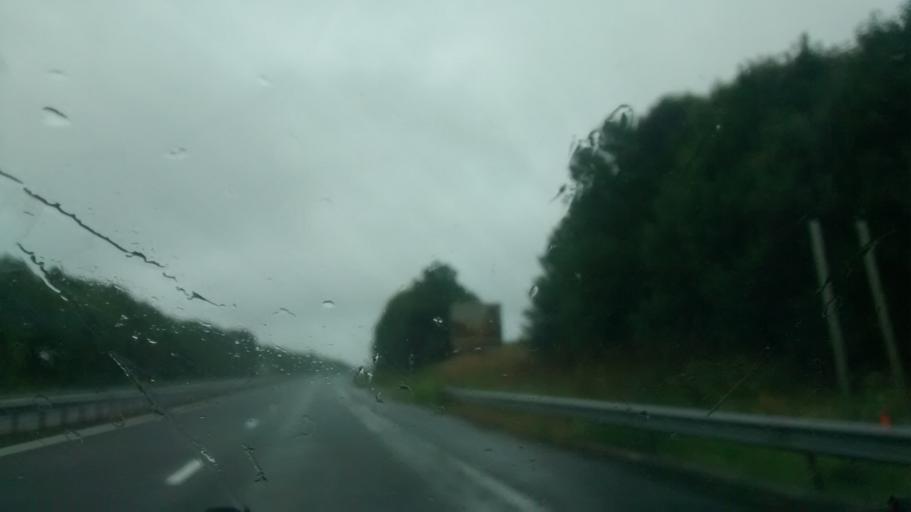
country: FR
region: Lower Normandy
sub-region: Departement de la Manche
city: Saint-James
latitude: 48.4749
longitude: -1.3275
